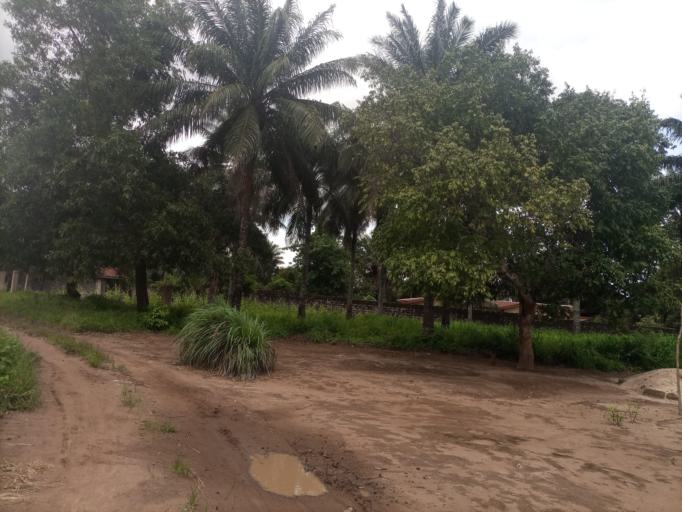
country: SL
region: Northern Province
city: Masoyila
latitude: 8.5940
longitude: -13.1645
